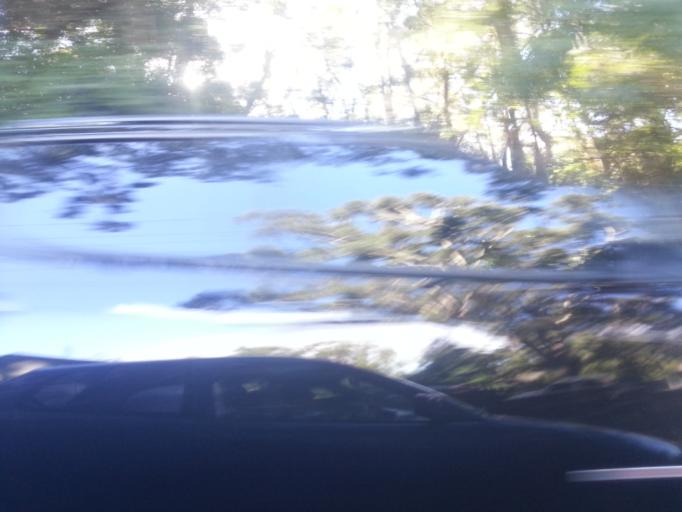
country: AU
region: New South Wales
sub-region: Wollongong
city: Mount Ousley
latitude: -34.3953
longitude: 150.8609
